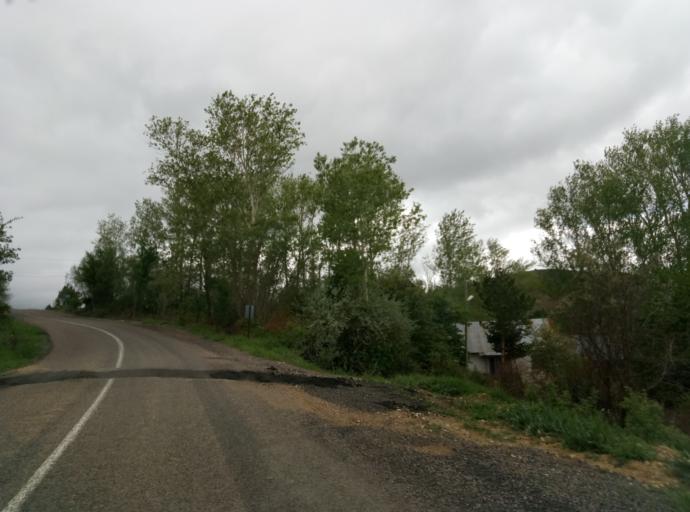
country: TR
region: Sivas
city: Aksu
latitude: 40.1883
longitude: 37.9372
